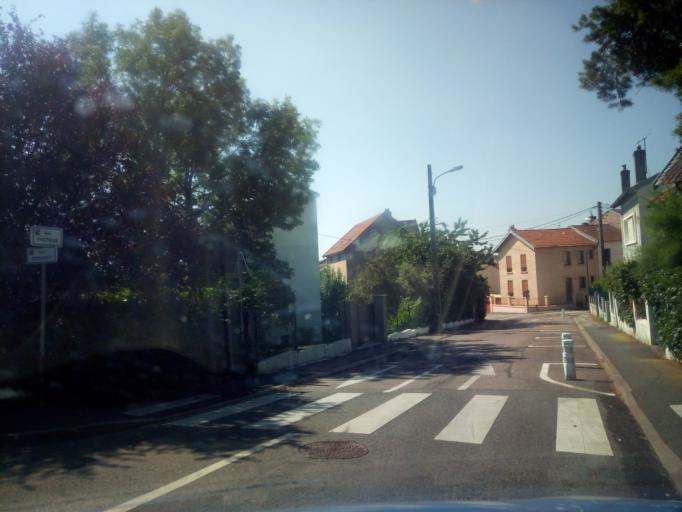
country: FR
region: Lorraine
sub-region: Departement de Meurthe-et-Moselle
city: Saint-Max
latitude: 48.7044
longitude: 6.2078
